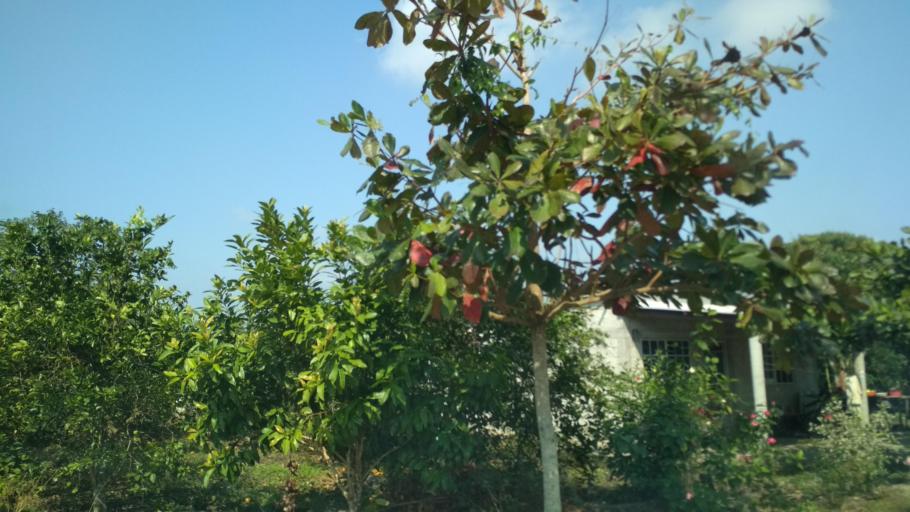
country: MX
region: Puebla
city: San Jose Acateno
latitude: 20.2056
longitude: -97.1784
